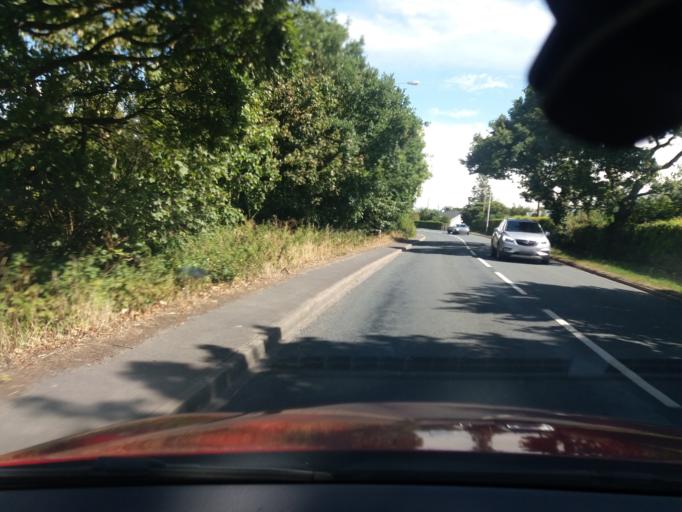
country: GB
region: England
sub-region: Lancashire
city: Euxton
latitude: 53.6619
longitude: -2.7221
